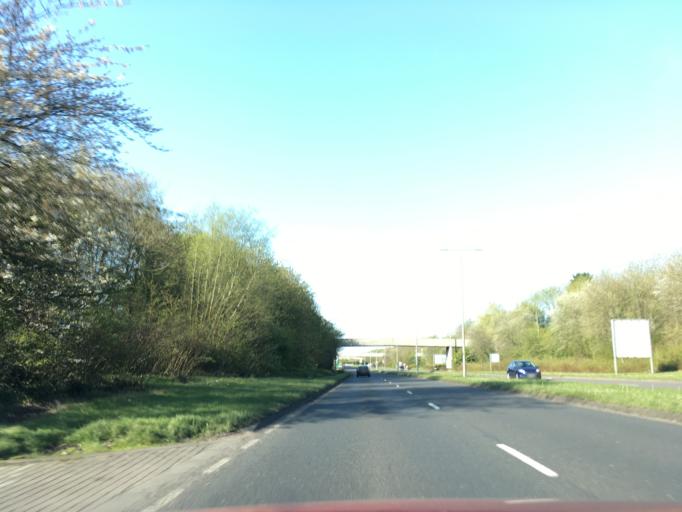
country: GB
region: England
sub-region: Milton Keynes
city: Milton Keynes
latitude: 52.0486
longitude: -0.7532
